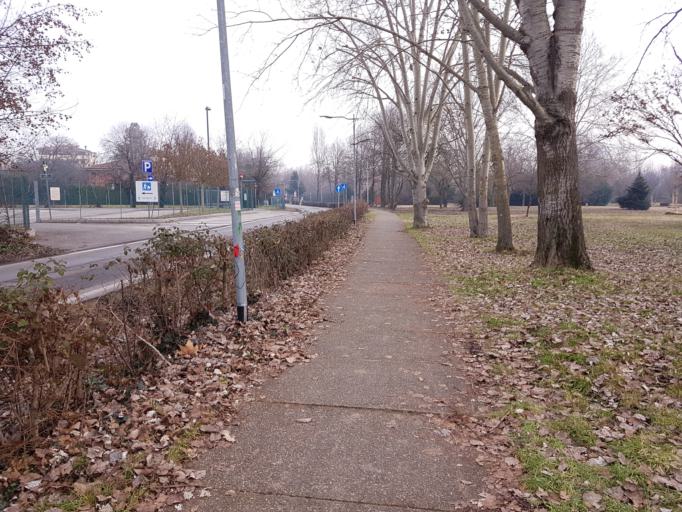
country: IT
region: Emilia-Romagna
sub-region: Provincia di Bologna
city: Quarto Inferiore
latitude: 44.5088
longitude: 11.3856
